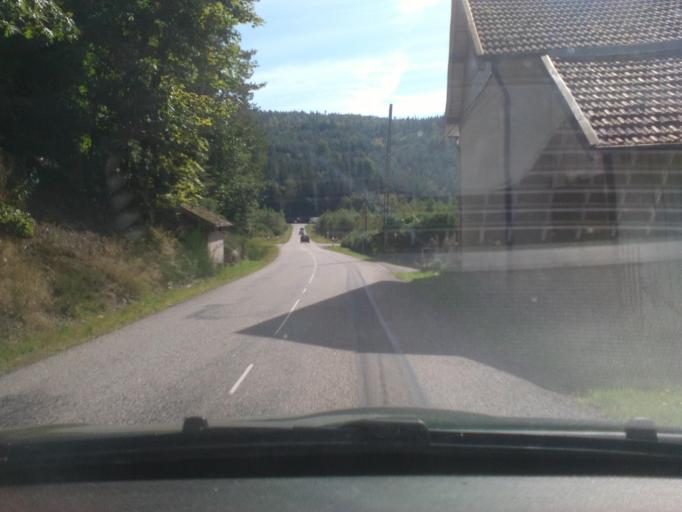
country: FR
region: Lorraine
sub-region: Departement des Vosges
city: Bruyeres
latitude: 48.2627
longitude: 6.7951
